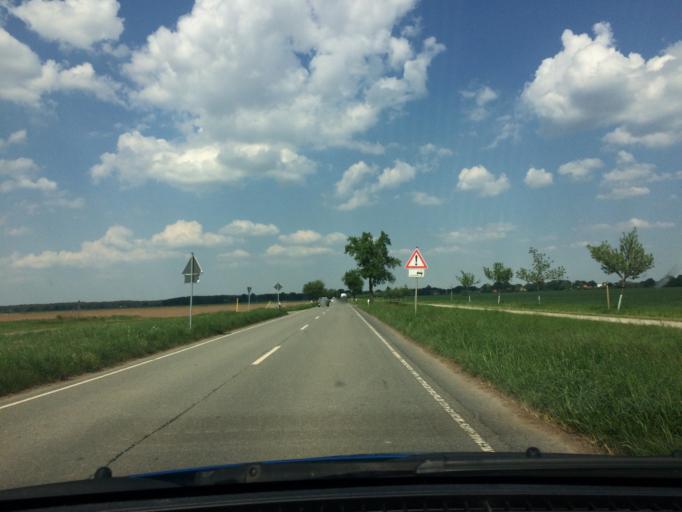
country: DE
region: Lower Saxony
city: Neu Darchau
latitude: 53.2485
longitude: 10.9055
